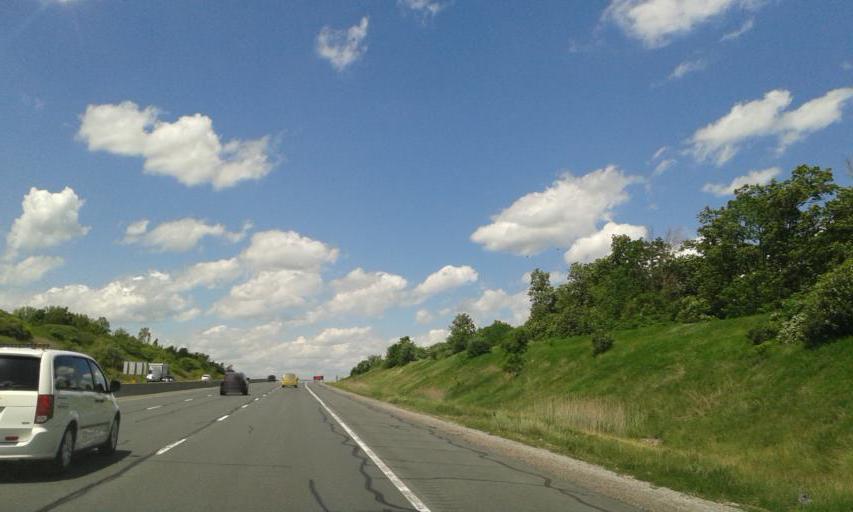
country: CA
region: Ontario
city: Burlington
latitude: 43.3629
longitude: -79.8319
